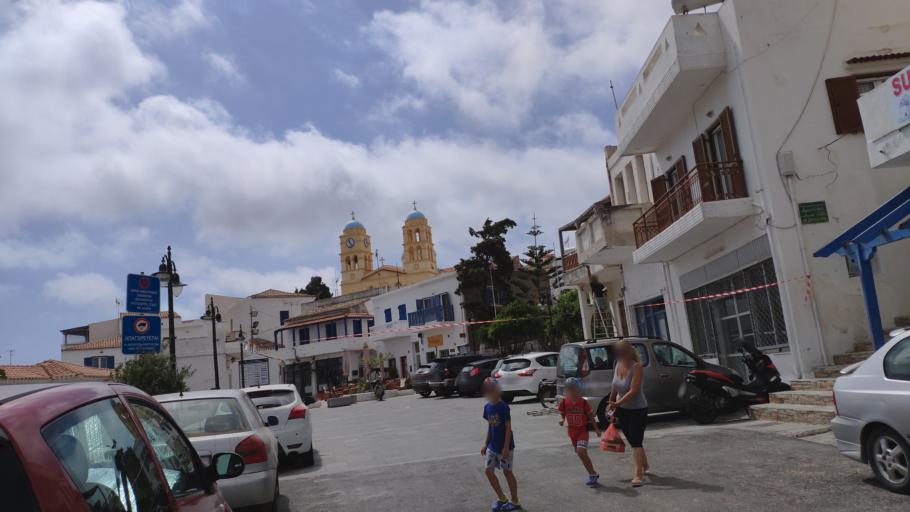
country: GR
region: South Aegean
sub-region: Nomos Kykladon
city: Kythnos
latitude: 37.3835
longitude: 24.4302
